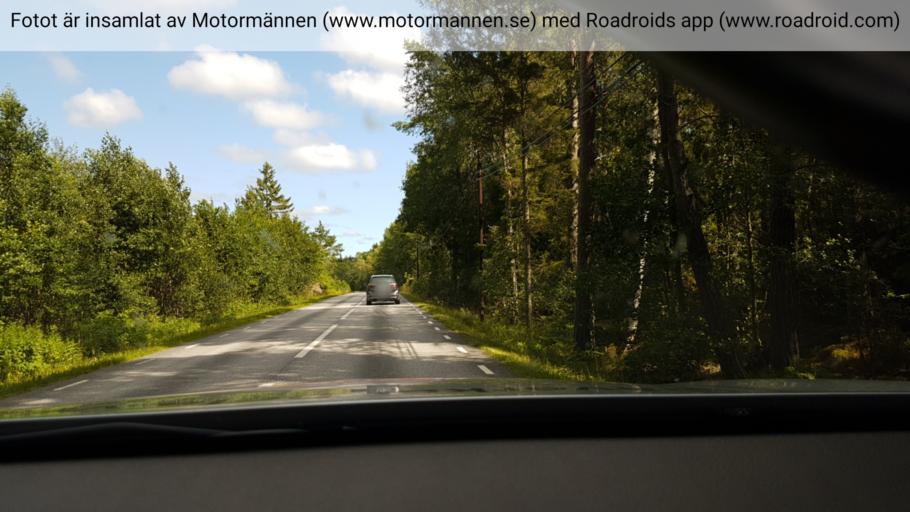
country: SE
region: Stockholm
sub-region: Norrtalje Kommun
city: Arno
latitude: 60.0780
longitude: 18.7799
